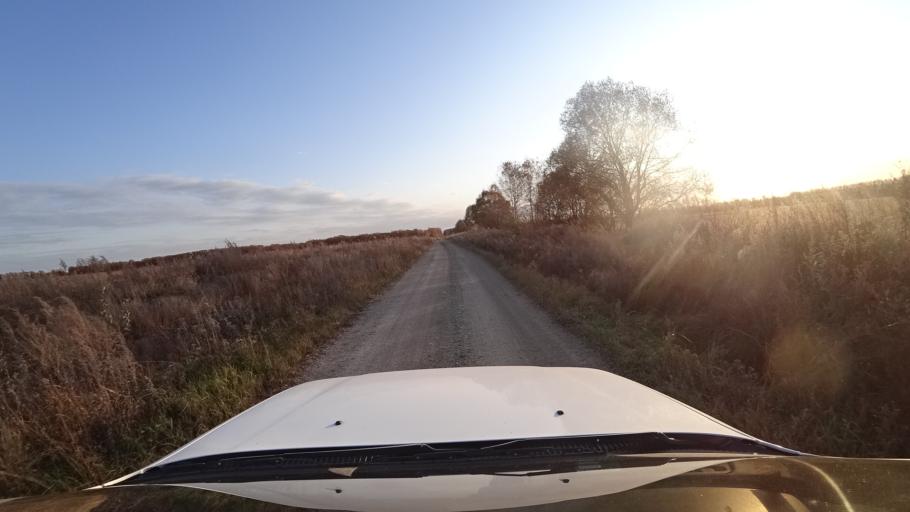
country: RU
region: Primorskiy
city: Lazo
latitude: 45.8108
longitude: 133.6081
